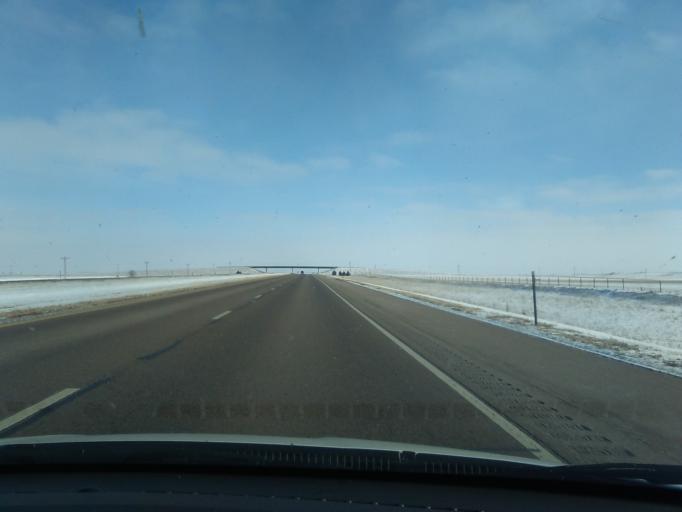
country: US
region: Nebraska
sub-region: Kimball County
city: Kimball
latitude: 41.1917
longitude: -103.8054
